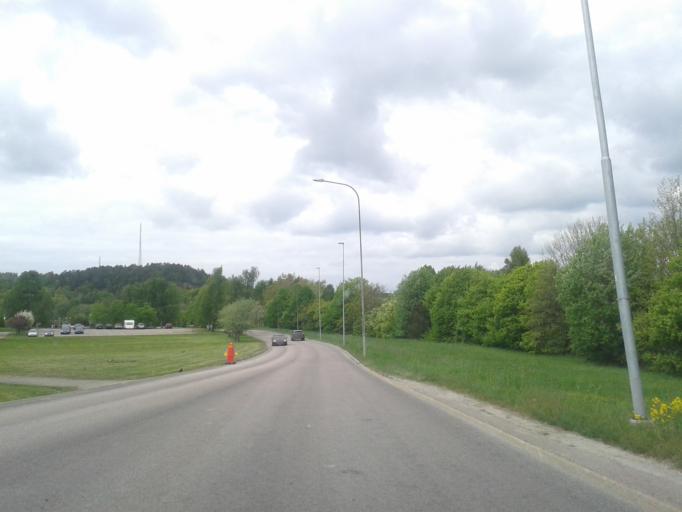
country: SE
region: Vaestra Goetaland
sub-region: Kungalvs Kommun
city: Kungalv
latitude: 57.8718
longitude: 11.9660
